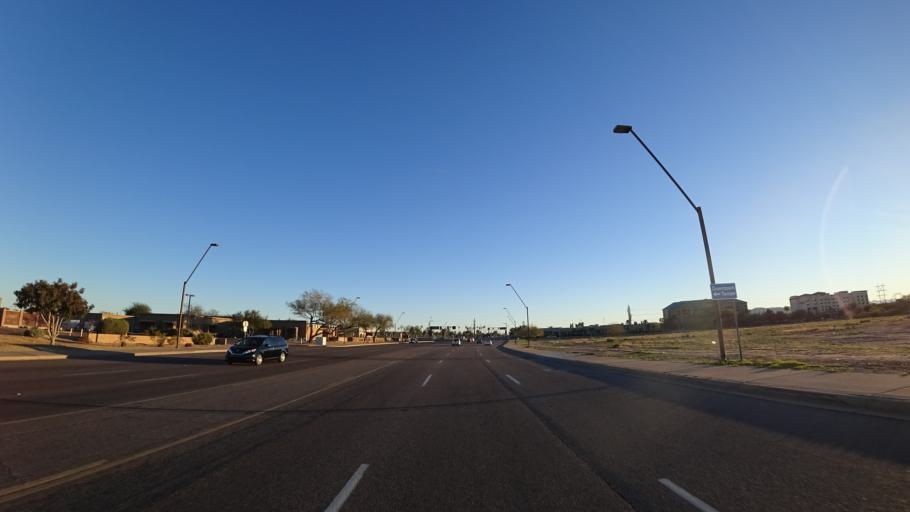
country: US
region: Arizona
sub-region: Maricopa County
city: Tempe Junction
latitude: 33.4313
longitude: -111.9612
